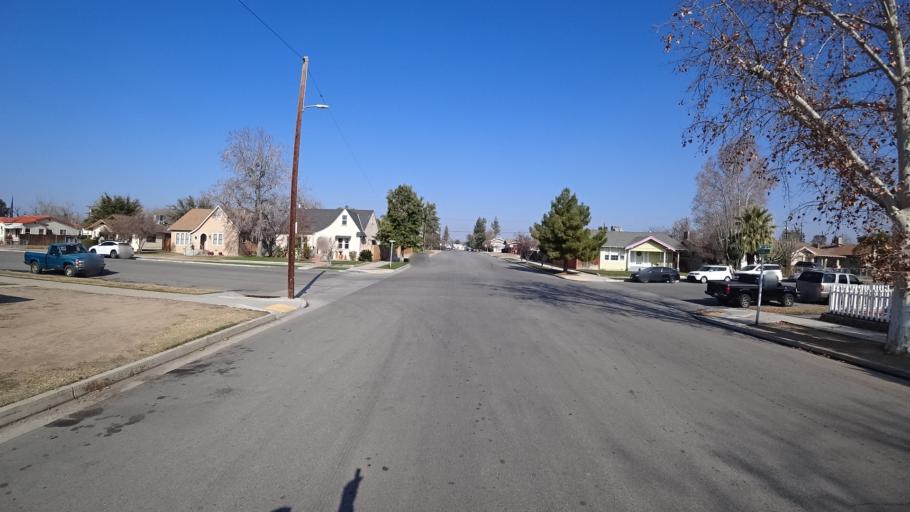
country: US
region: California
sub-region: Kern County
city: Bakersfield
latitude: 35.3875
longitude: -118.9908
